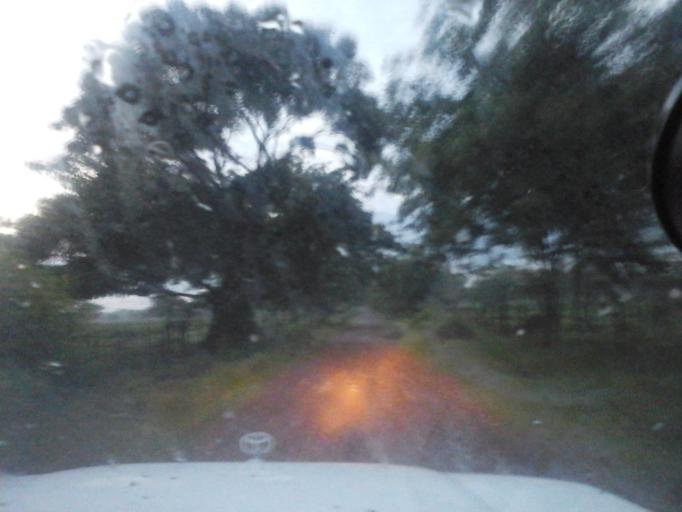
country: CO
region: Cesar
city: Agustin Codazzi
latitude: 10.1552
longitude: -73.2172
